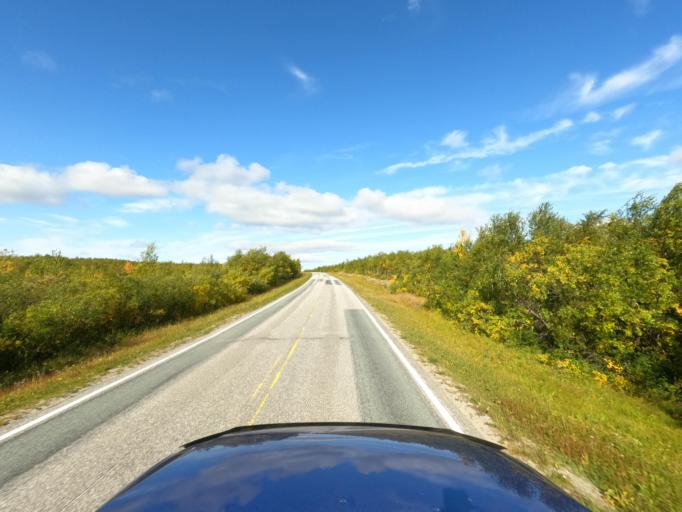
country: NO
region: Finnmark Fylke
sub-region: Karasjok
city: Karasjohka
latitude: 69.5844
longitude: 25.3481
